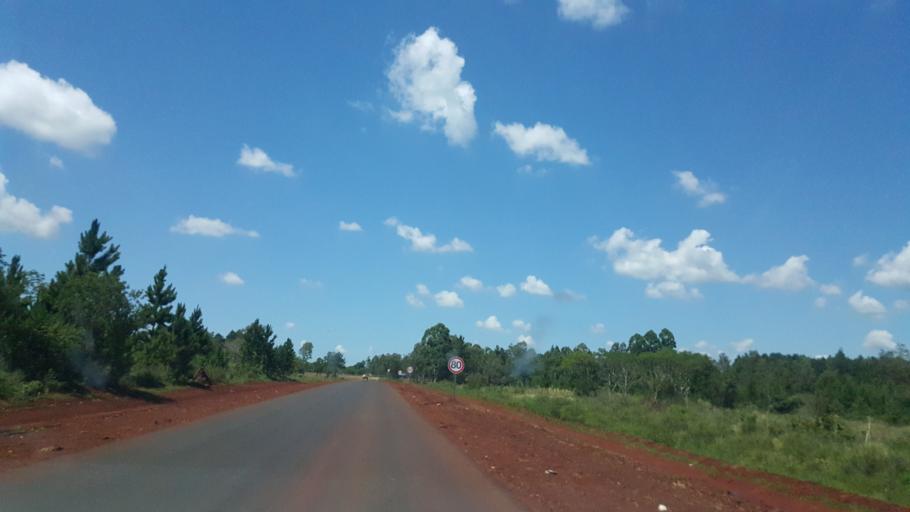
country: AR
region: Corrientes
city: Santo Tome
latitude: -28.5036
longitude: -56.0561
